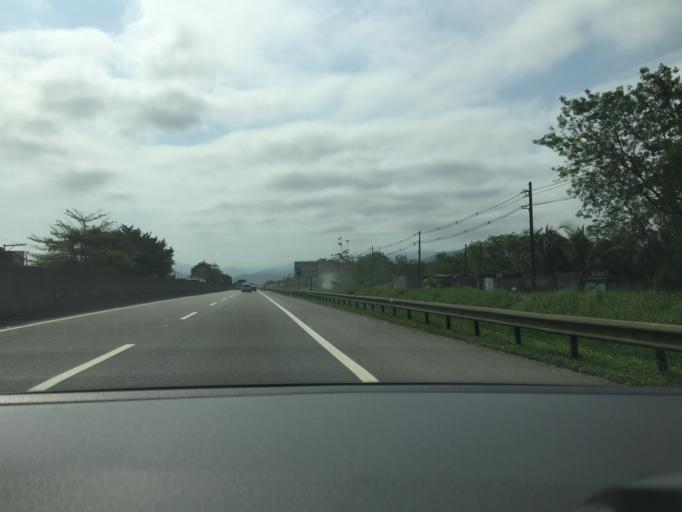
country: BR
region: Sao Paulo
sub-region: Guaruja
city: Guaruja
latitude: -23.9572
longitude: -46.2746
